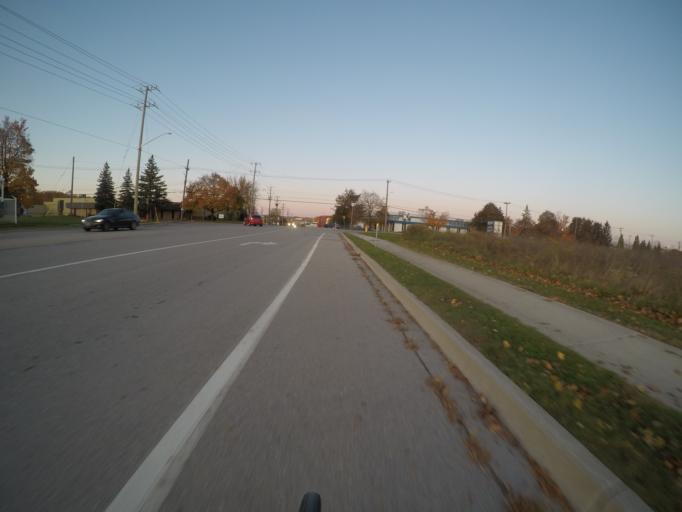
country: CA
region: Ontario
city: Kitchener
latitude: 43.4096
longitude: -80.4402
